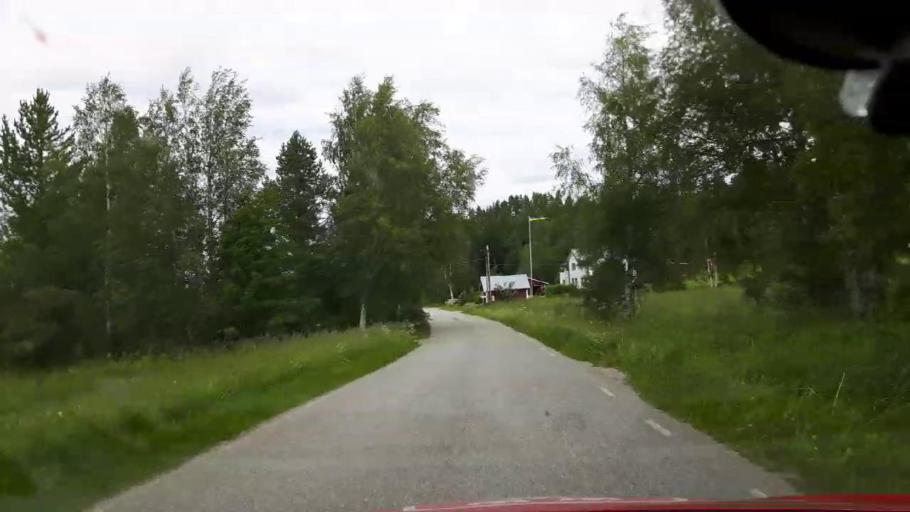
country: SE
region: Jaemtland
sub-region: Braecke Kommun
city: Braecke
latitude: 62.8795
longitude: 15.2755
